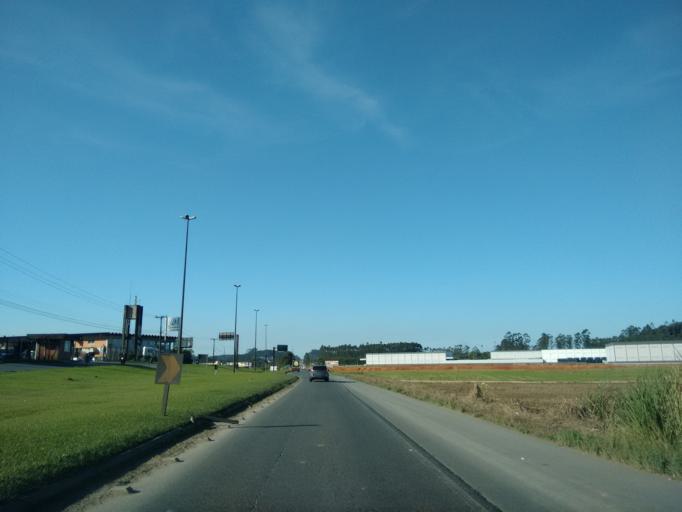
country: BR
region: Santa Catarina
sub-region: Guaramirim
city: Guaramirim
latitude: -26.4680
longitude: -48.9623
